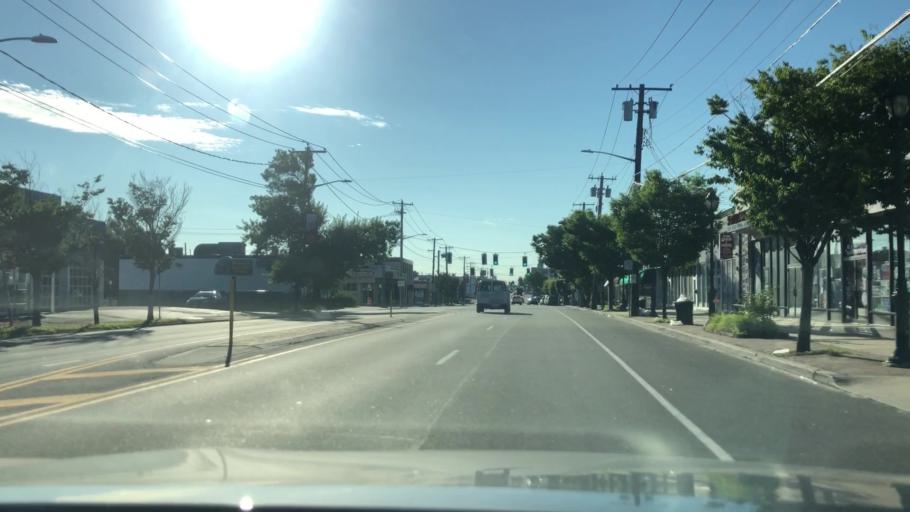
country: US
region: New York
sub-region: Nassau County
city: Franklin Square
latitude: 40.7079
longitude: -73.6804
